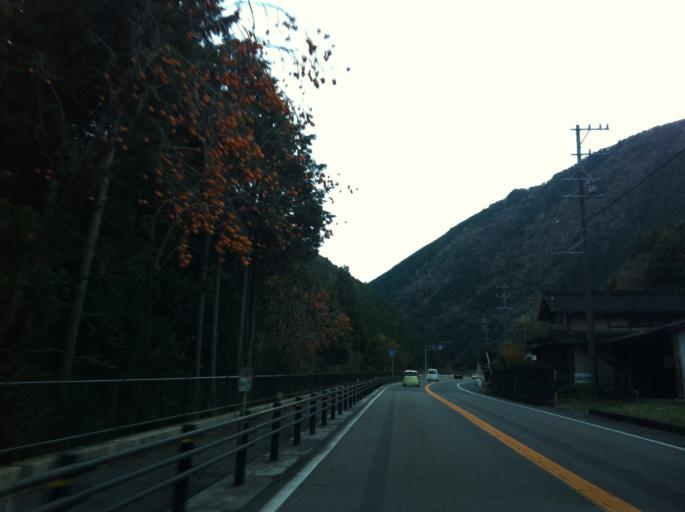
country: JP
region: Gifu
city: Mitake
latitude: 35.5904
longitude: 137.1707
